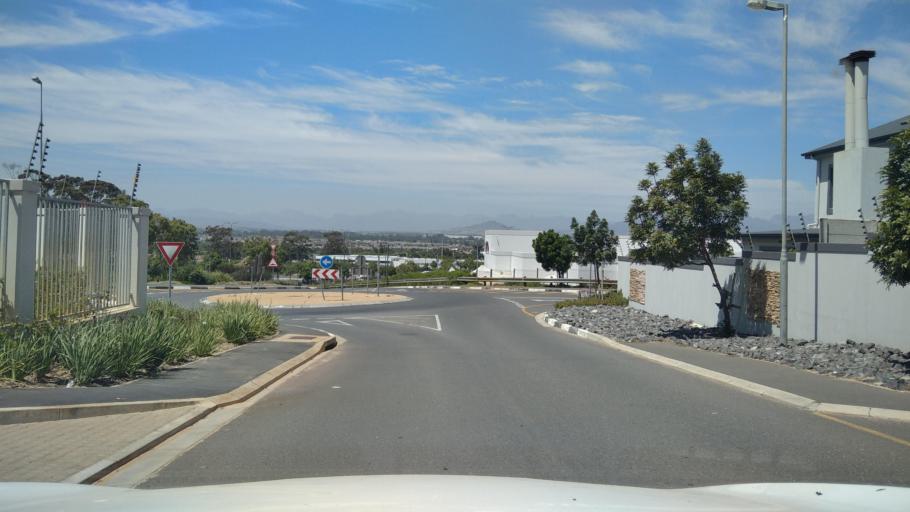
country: ZA
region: Western Cape
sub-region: City of Cape Town
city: Kraaifontein
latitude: -33.8392
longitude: 18.6940
